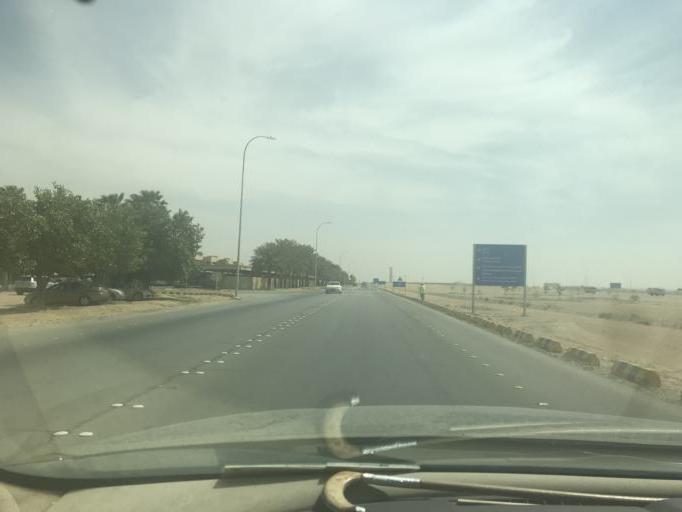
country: SA
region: Ar Riyad
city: Riyadh
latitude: 24.9782
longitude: 46.6871
